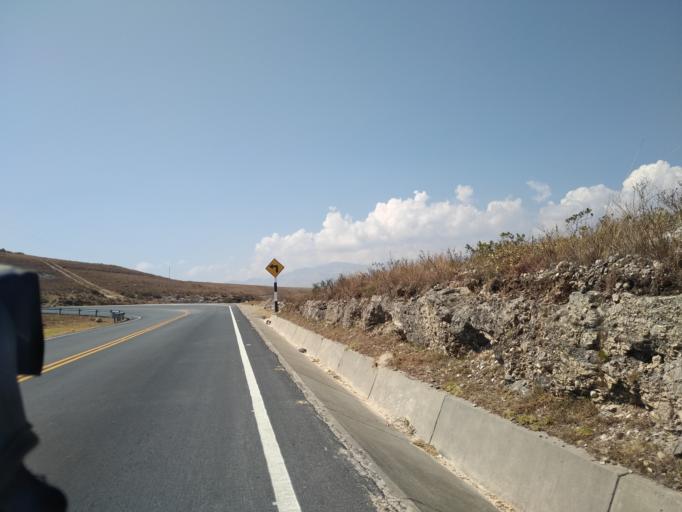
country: PE
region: Cajamarca
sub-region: Provincia de Cajamarca
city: Llacanora
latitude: -7.2066
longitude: -78.3873
